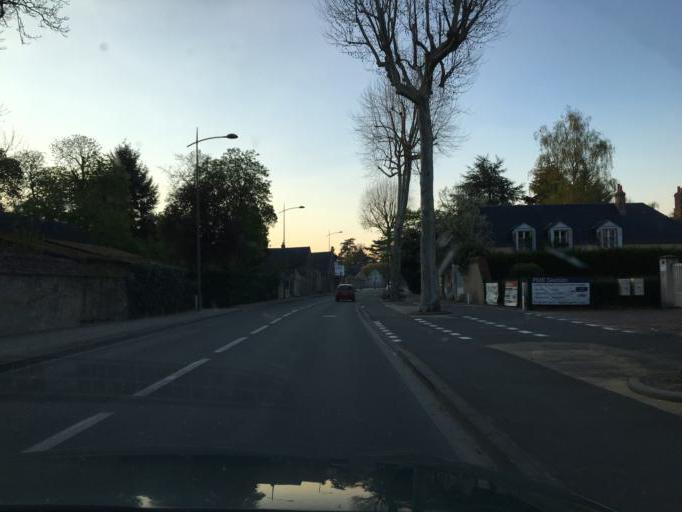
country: FR
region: Centre
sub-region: Departement du Loiret
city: Saint-Jean-le-Blanc
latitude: 47.8810
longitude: 1.9333
